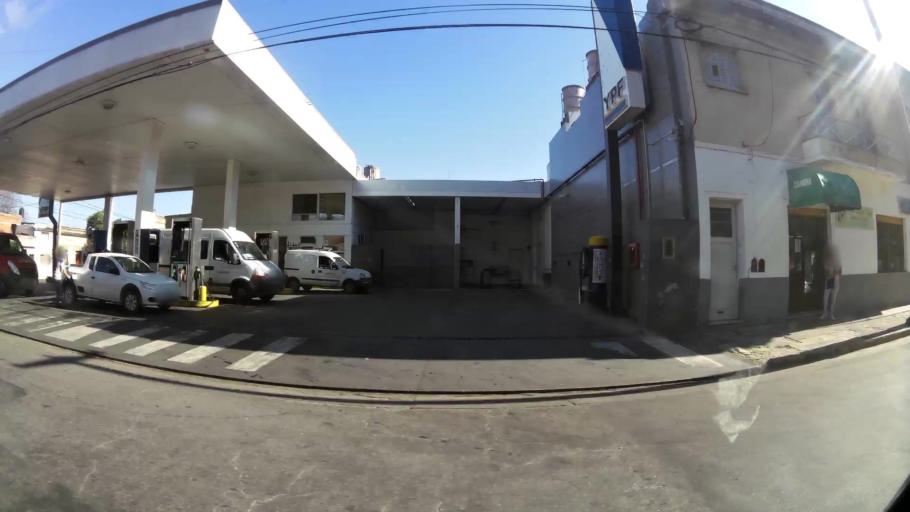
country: AR
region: Cordoba
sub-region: Departamento de Capital
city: Cordoba
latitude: -31.4254
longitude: -64.1492
